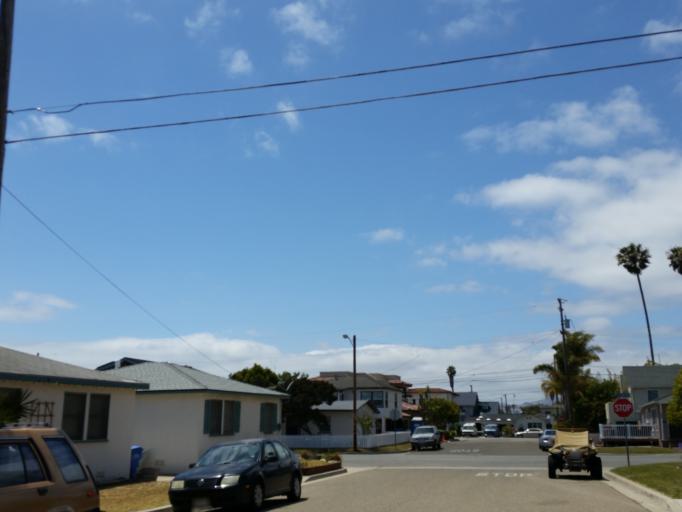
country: US
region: California
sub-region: San Luis Obispo County
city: Pismo Beach
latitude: 35.1538
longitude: -120.6695
